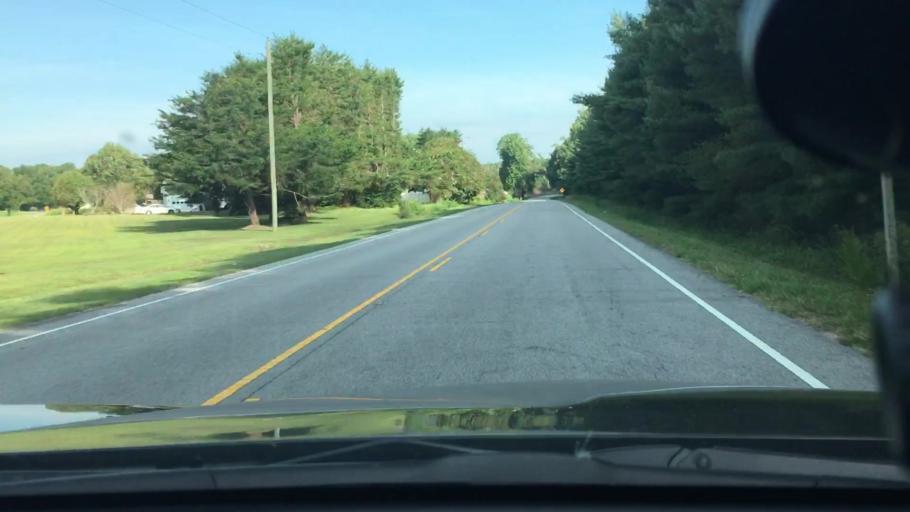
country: US
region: North Carolina
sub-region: Edgecombe County
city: Pinetops
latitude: 35.7371
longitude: -77.5359
